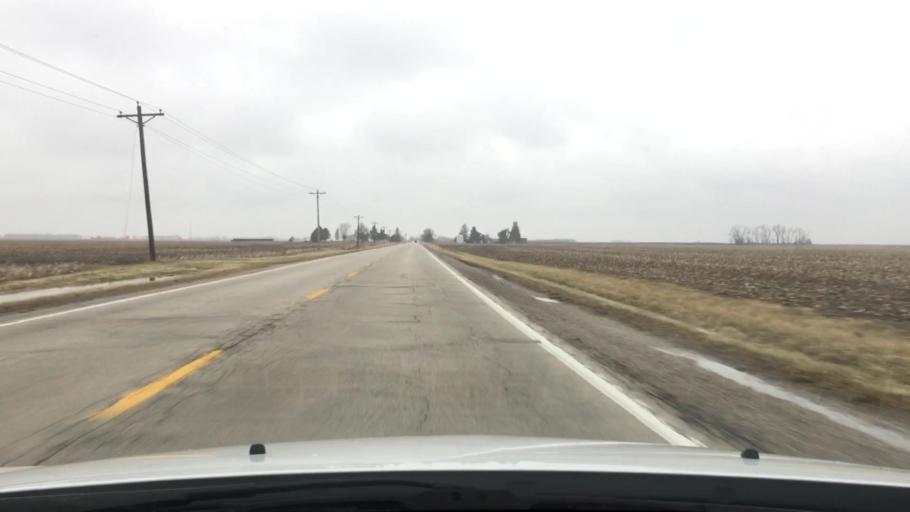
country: US
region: Illinois
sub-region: Iroquois County
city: Watseka
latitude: 40.8905
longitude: -87.6969
